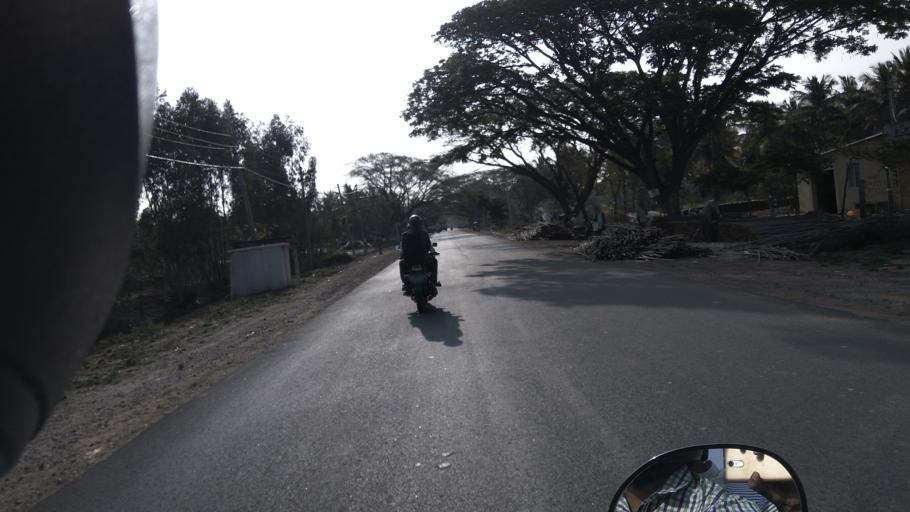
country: IN
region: Karnataka
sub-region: Kolar
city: Kolar
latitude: 13.1152
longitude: 78.1838
